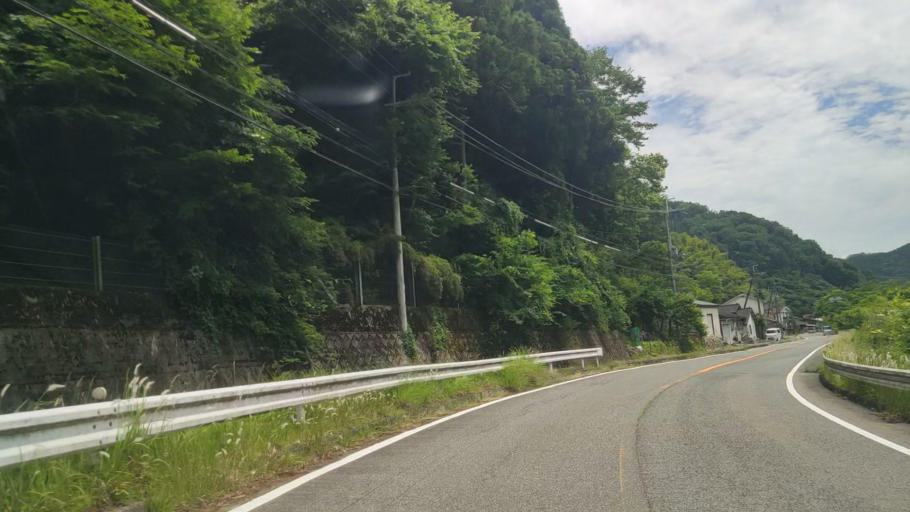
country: JP
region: Hyogo
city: Yamazakicho-nakabirose
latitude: 35.0930
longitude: 134.3625
